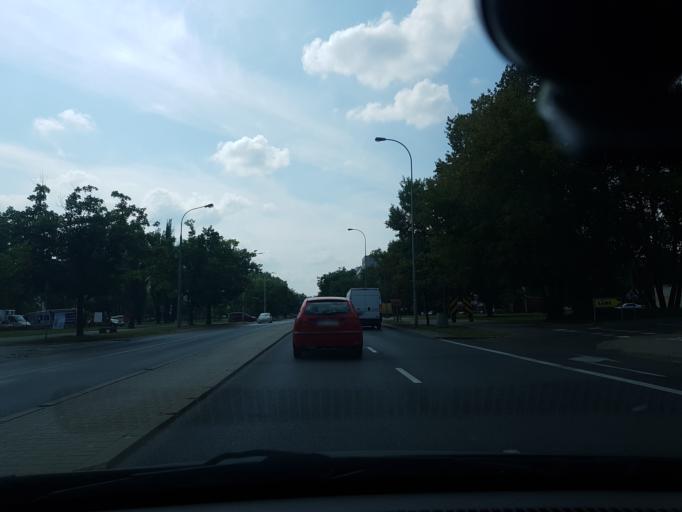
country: PL
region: Masovian Voivodeship
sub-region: Warszawa
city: Bielany
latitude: 52.2882
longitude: 20.9327
